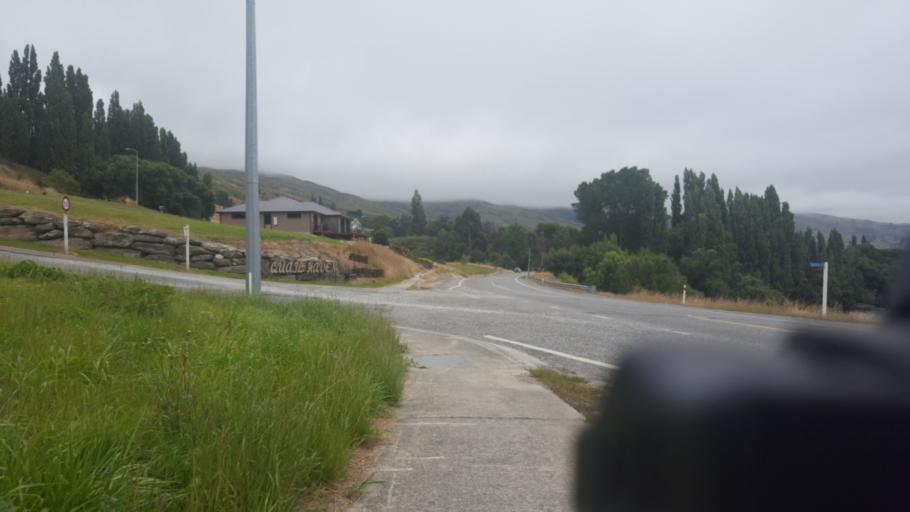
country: NZ
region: Otago
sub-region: Queenstown-Lakes District
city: Kingston
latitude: -45.5344
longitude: 169.3019
